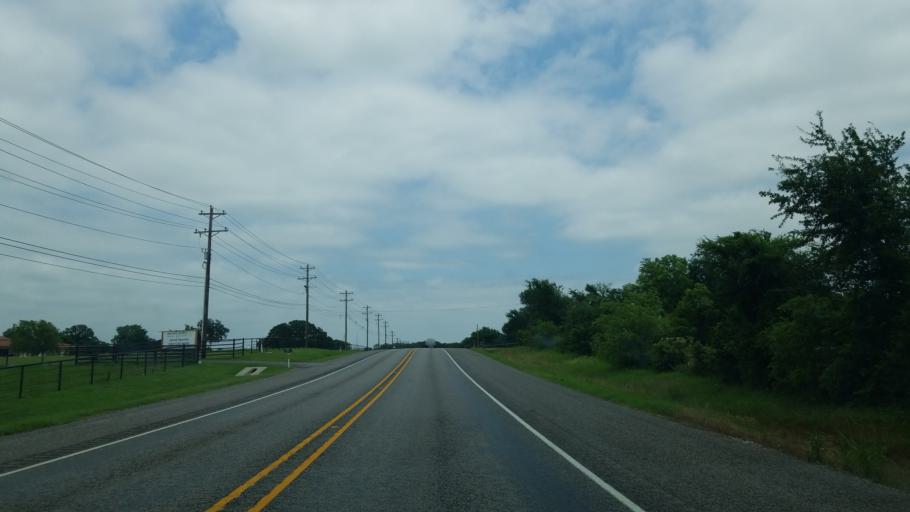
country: US
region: Texas
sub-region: Denton County
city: Aubrey
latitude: 33.3045
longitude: -97.0194
